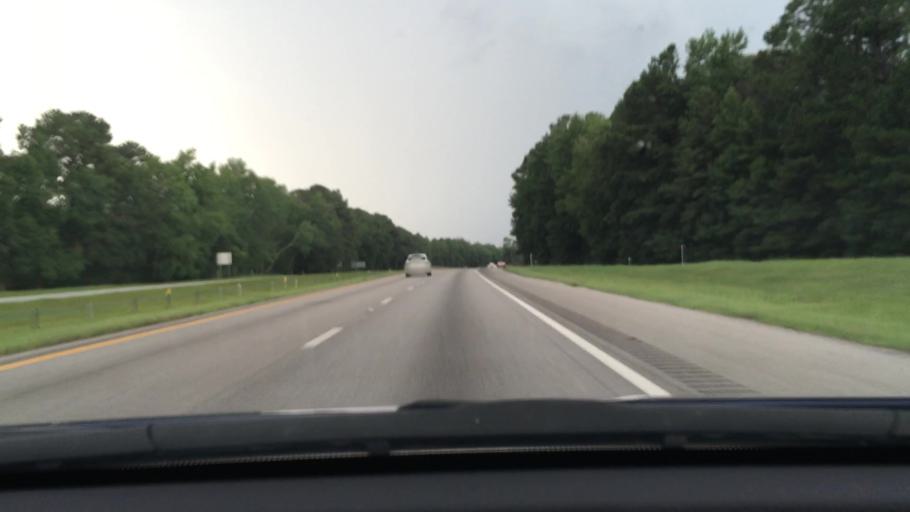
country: US
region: South Carolina
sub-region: Kershaw County
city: Elgin
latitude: 34.1414
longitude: -80.7525
